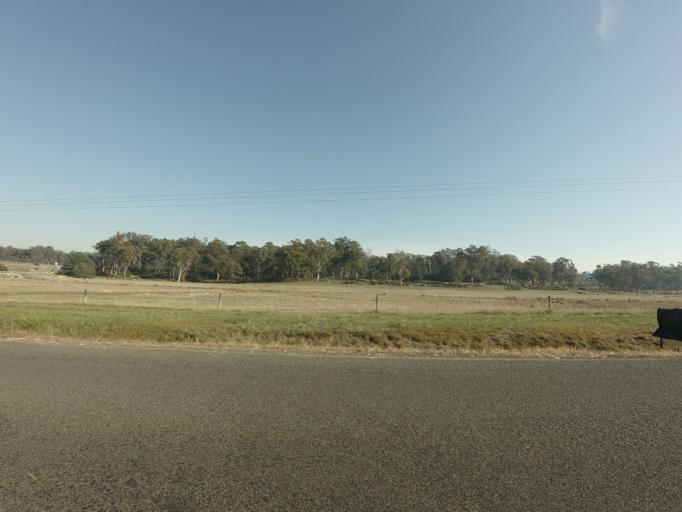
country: AU
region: Tasmania
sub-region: Northern Midlands
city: Longford
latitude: -41.5513
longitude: 146.9900
